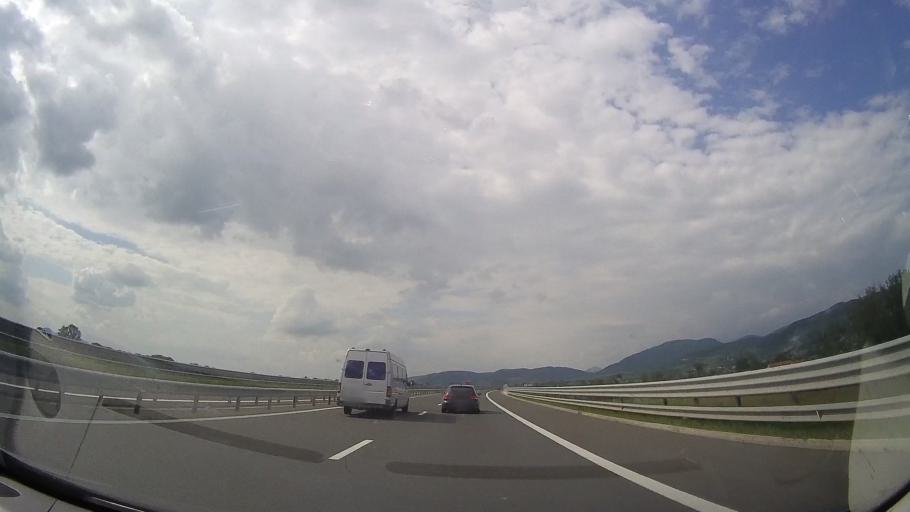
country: RO
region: Hunedoara
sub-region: Oras Simeria
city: Simeria
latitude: 45.8578
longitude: 23.0295
